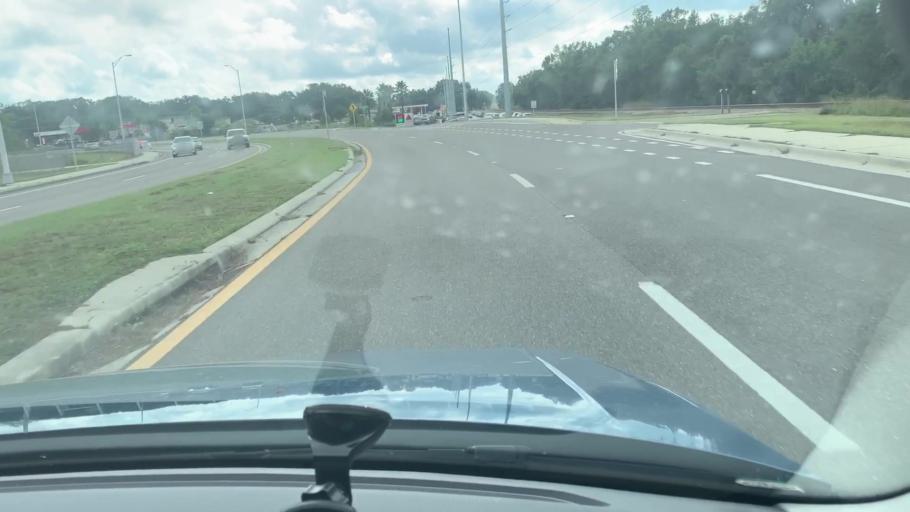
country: US
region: Florida
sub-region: Polk County
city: Kathleen
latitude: 28.1004
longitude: -82.0095
